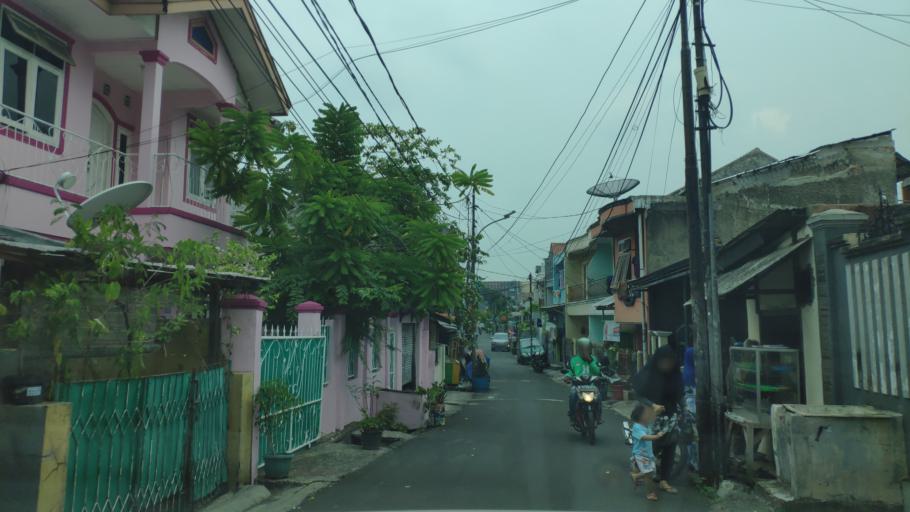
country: ID
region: Jakarta Raya
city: Jakarta
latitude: -6.1930
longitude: 106.7992
